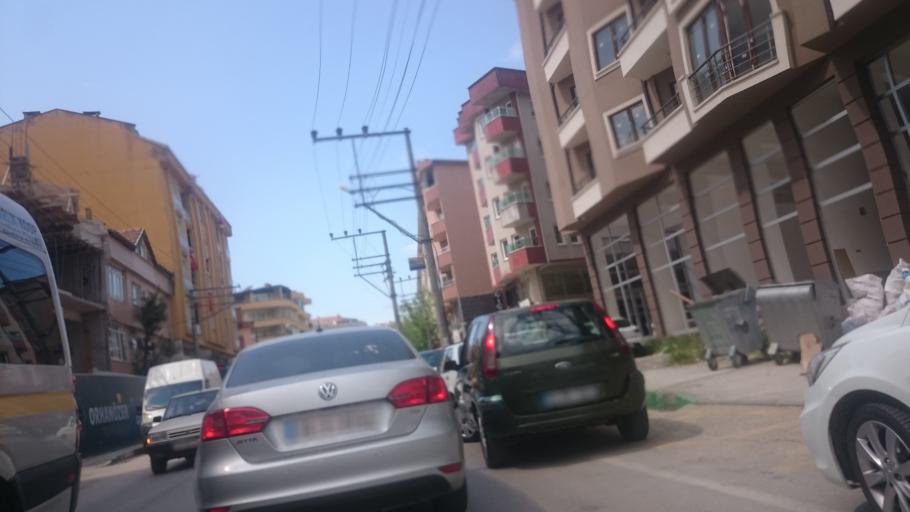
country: TR
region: Bursa
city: Yildirim
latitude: 40.2218
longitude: 28.9883
